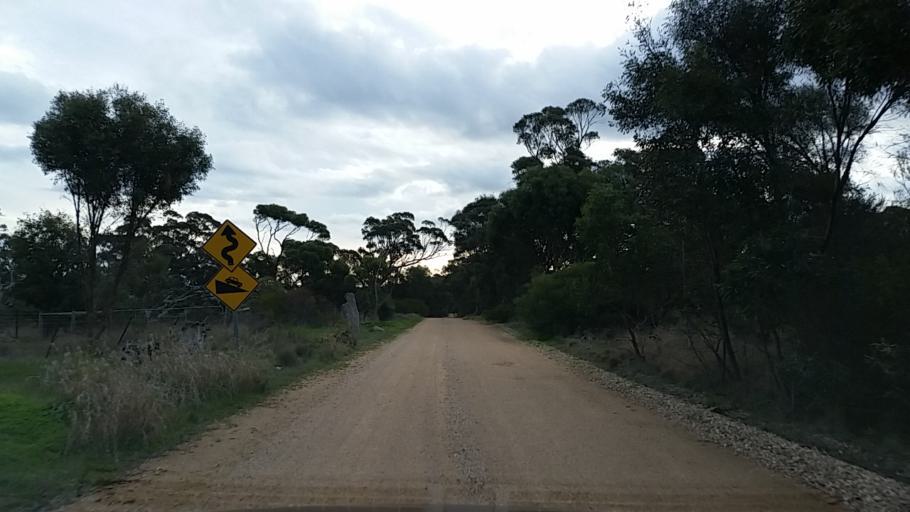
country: AU
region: South Australia
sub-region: Mount Barker
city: Callington
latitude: -35.0000
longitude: 139.0594
